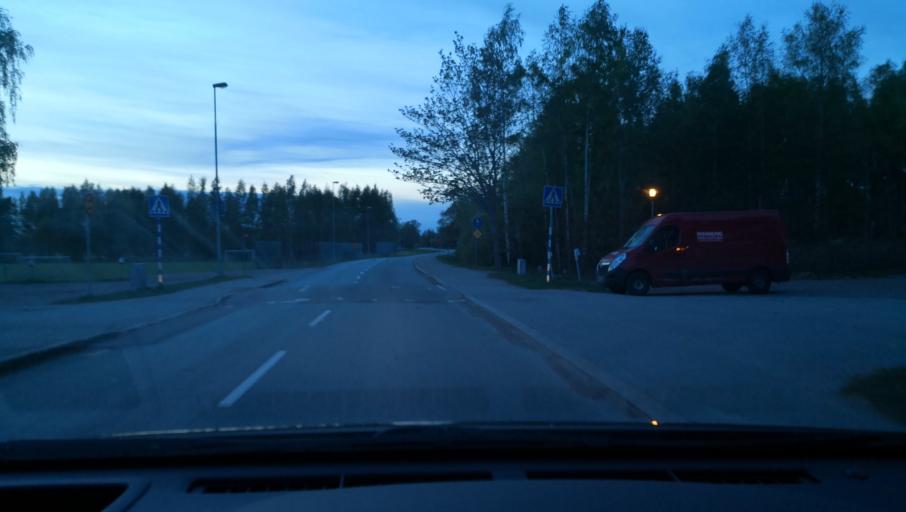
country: SE
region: OErebro
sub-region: Lekebergs Kommun
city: Fjugesta
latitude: 59.0274
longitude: 14.8659
